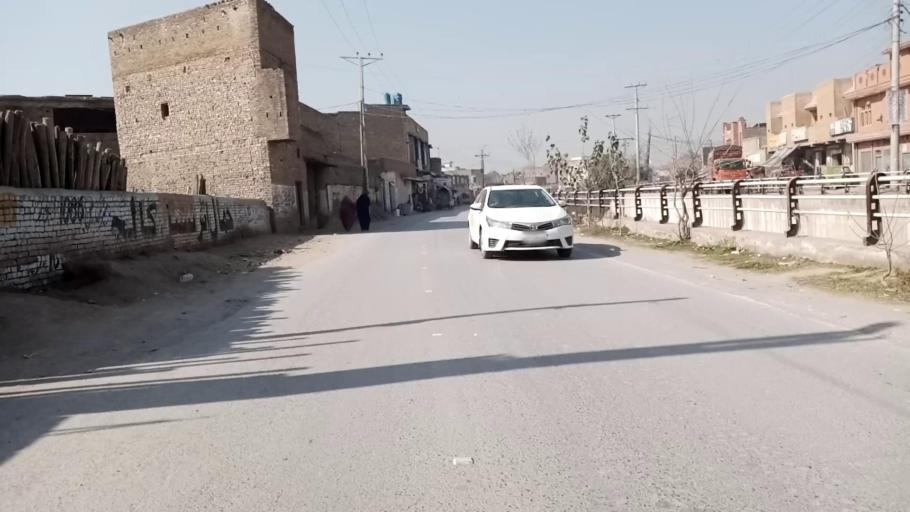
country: PK
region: Khyber Pakhtunkhwa
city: Peshawar
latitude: 33.9727
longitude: 71.5228
